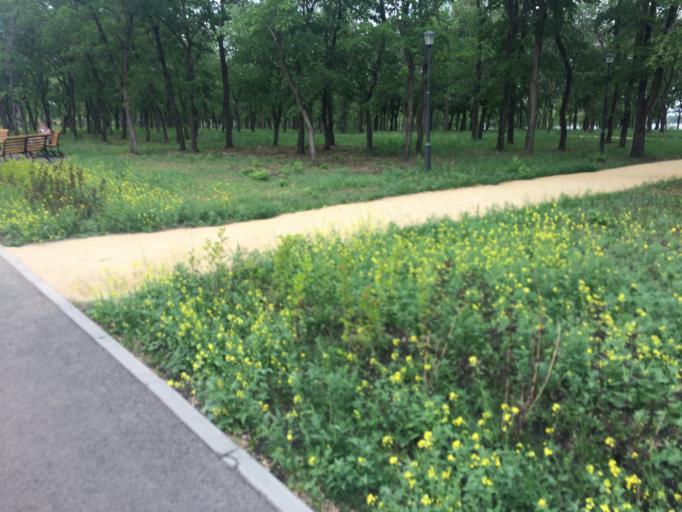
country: RU
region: Chelyabinsk
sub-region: Gorod Magnitogorsk
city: Magnitogorsk
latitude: 53.4025
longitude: 58.9921
